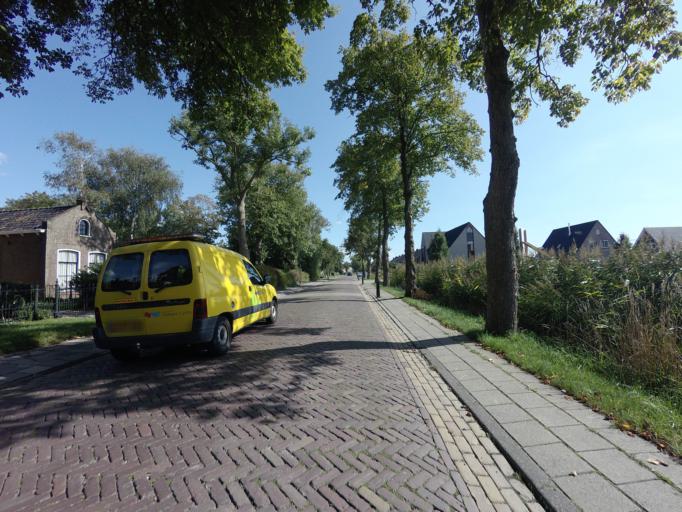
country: NL
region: Friesland
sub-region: Gemeente Littenseradiel
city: Makkum
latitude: 53.1009
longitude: 5.6438
